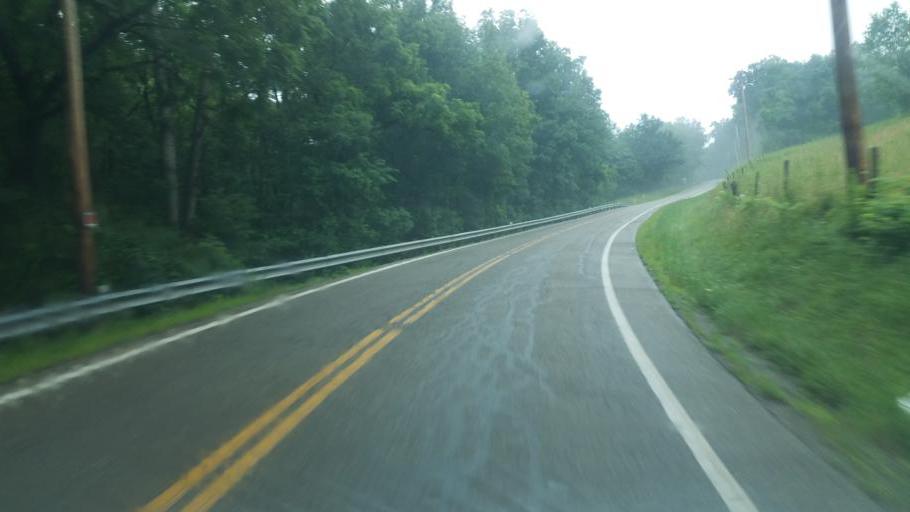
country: US
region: Ohio
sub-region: Carroll County
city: Carrollton
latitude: 40.4474
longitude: -81.0459
